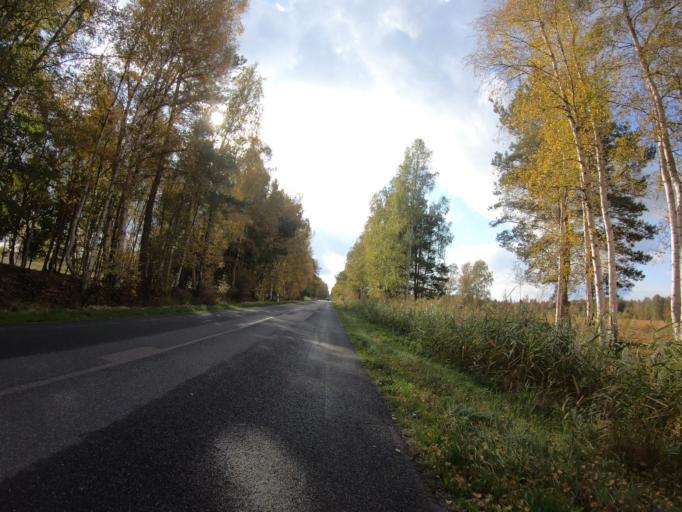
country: DE
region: Lower Saxony
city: Wahrenholz
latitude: 52.5764
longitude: 10.6368
